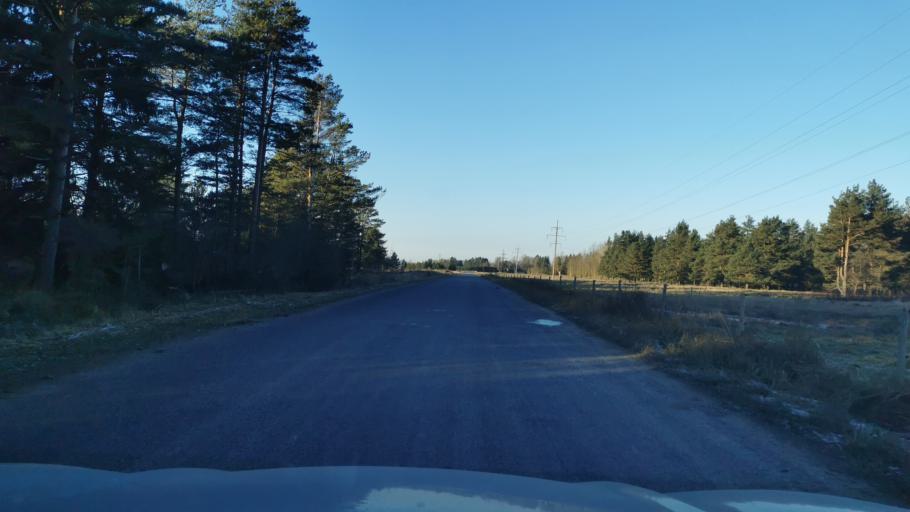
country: EE
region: Ida-Virumaa
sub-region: Puessi linn
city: Pussi
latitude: 59.3408
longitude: 27.0566
